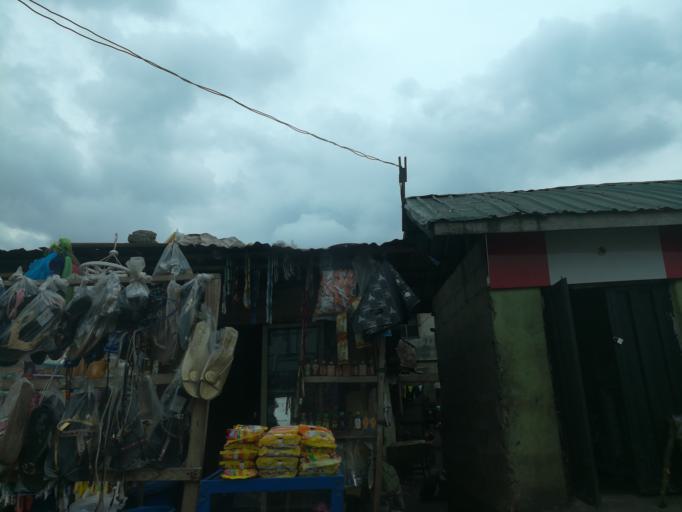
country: NG
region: Lagos
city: Ojota
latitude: 6.6115
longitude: 3.3974
